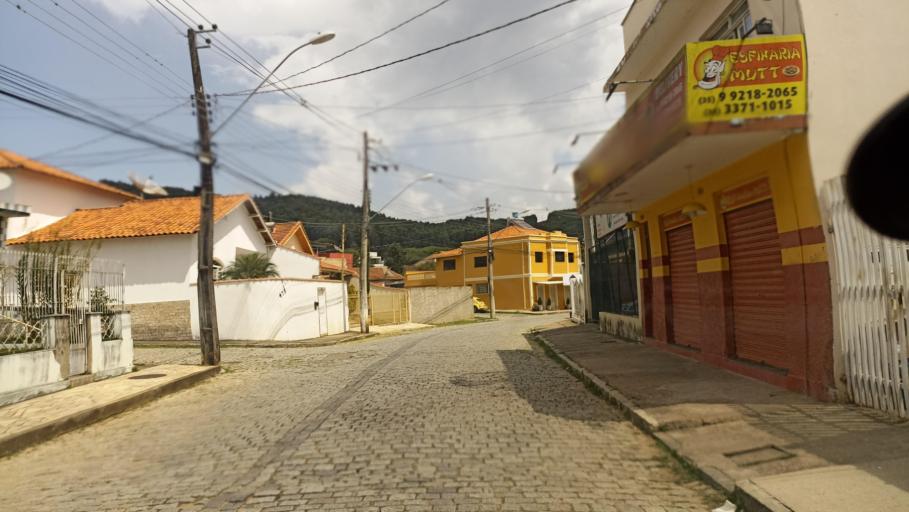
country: BR
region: Minas Gerais
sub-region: Passa Quatro
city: Passa Quatro
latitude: -22.3949
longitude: -44.9658
